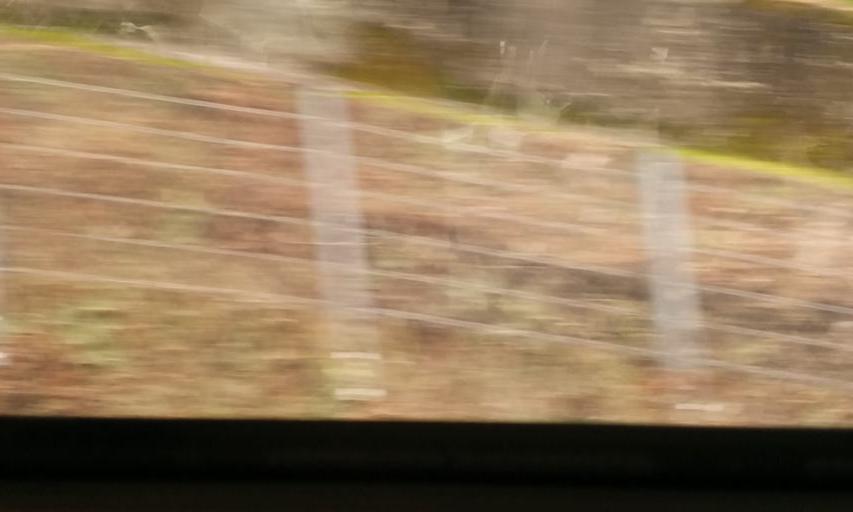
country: JP
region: Nagano
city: Ina
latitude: 35.7969
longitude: 137.6878
